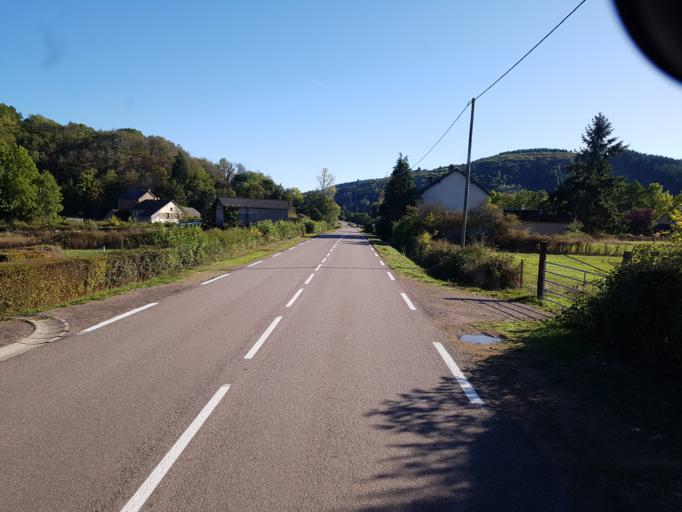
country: FR
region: Bourgogne
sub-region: Departement de Saone-et-Loire
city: Autun
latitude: 47.1012
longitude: 4.2310
